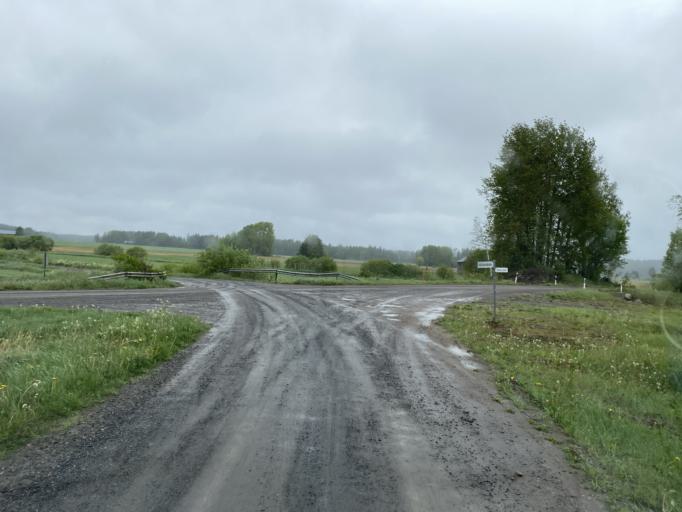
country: FI
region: Pirkanmaa
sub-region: Etelae-Pirkanmaa
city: Urjala
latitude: 60.9601
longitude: 23.5965
